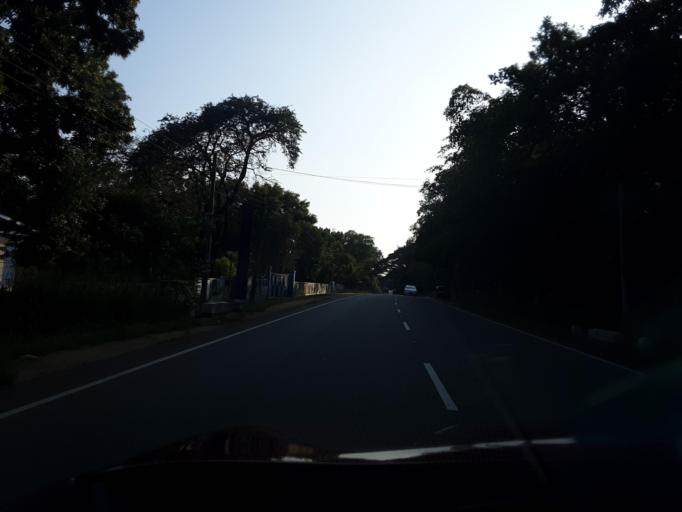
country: LK
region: Central
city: Sigiriya
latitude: 7.9836
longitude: 80.7198
